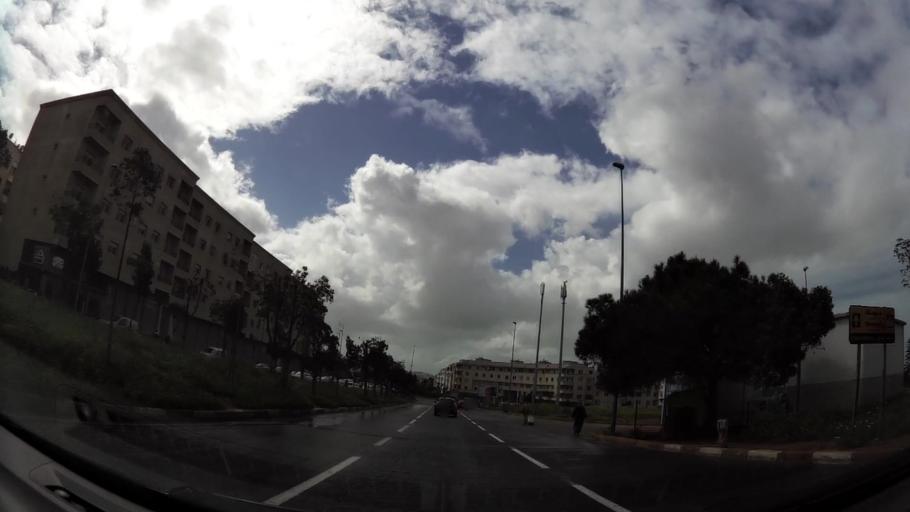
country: MA
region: Grand Casablanca
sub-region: Casablanca
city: Casablanca
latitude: 33.5316
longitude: -7.6464
